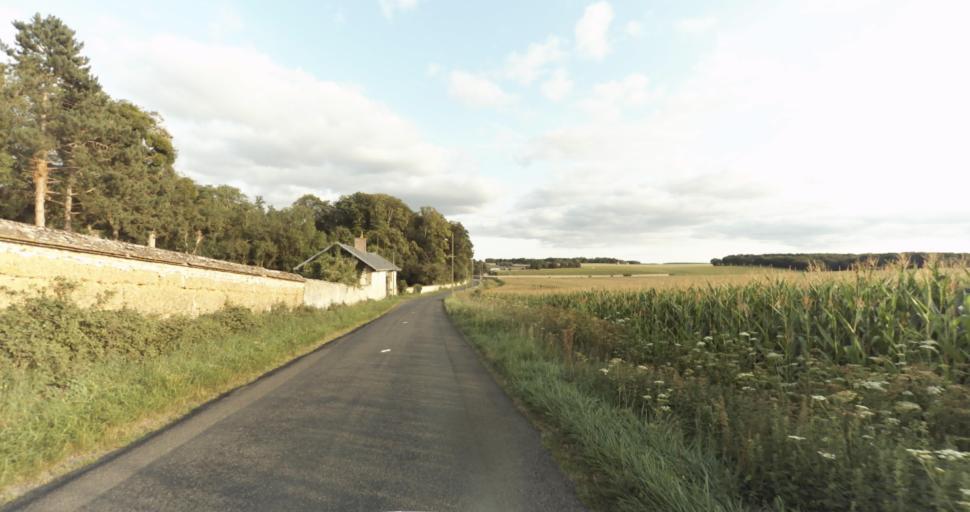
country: FR
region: Haute-Normandie
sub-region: Departement de l'Eure
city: Marcilly-sur-Eure
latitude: 48.8012
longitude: 1.3139
